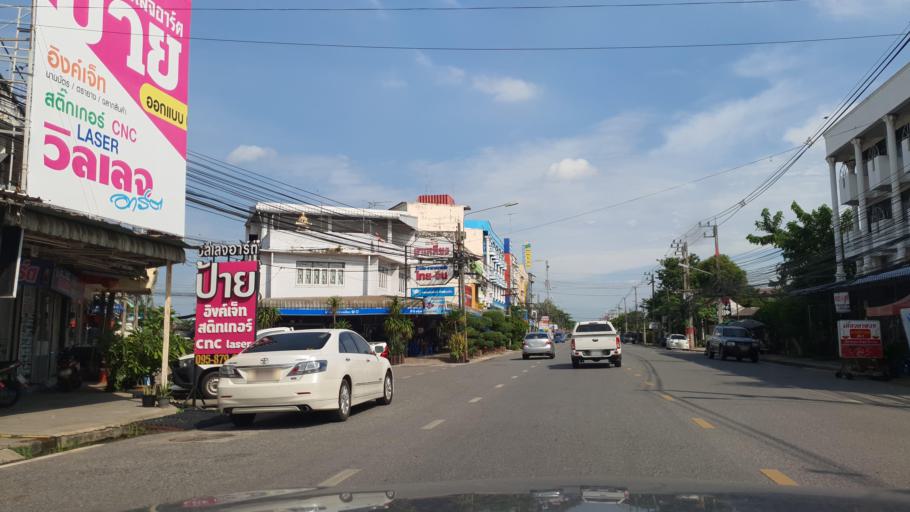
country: TH
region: Chachoengsao
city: Chachoengsao
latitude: 13.6875
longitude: 101.0648
